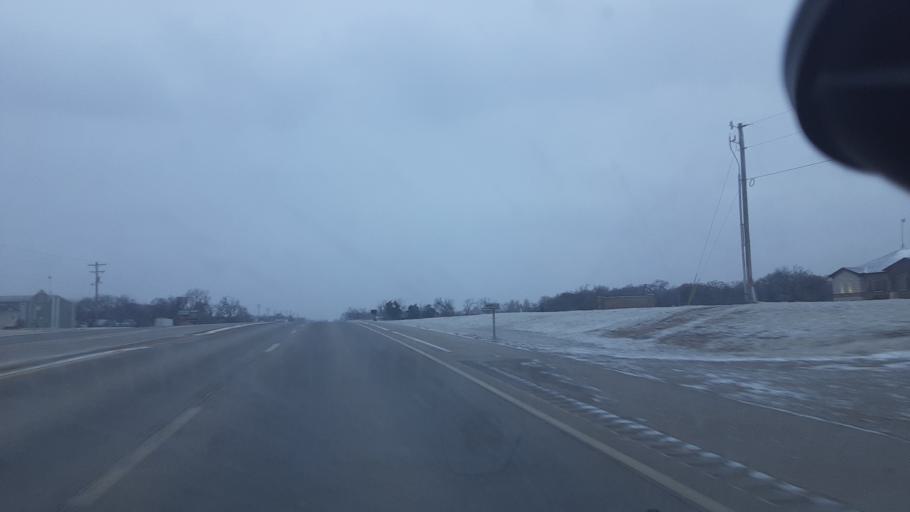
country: US
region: Oklahoma
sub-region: Payne County
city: Perkins
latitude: 35.9855
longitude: -97.0601
